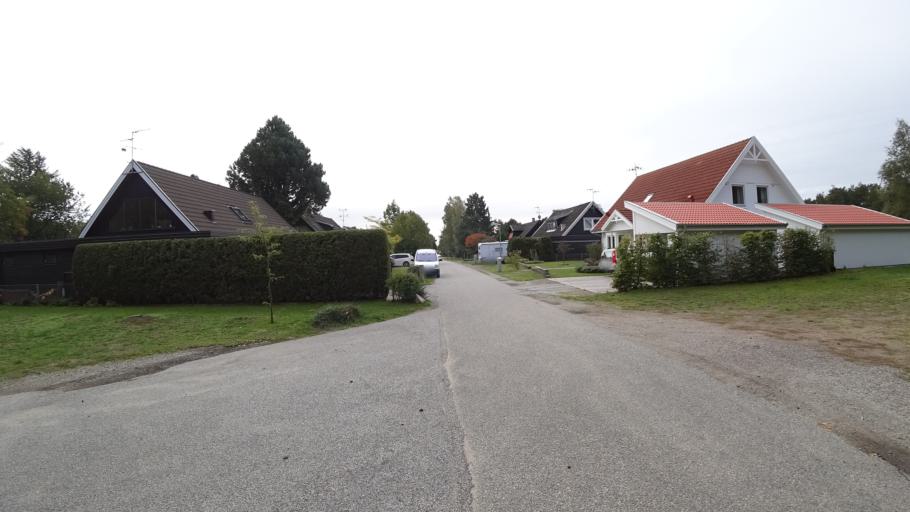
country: SE
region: Skane
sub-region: Kavlinge Kommun
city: Hofterup
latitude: 55.7973
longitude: 12.9787
